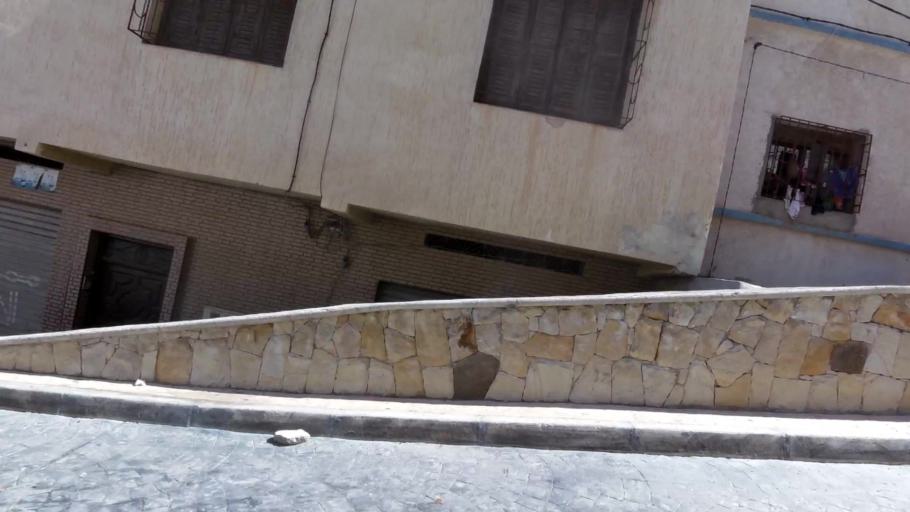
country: MA
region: Tanger-Tetouan
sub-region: Tetouan
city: Martil
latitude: 35.6822
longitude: -5.3220
